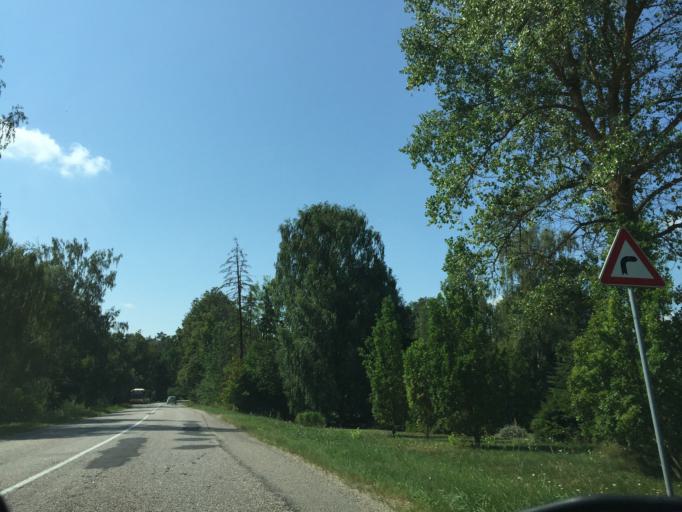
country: LV
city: Tervete
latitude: 56.4950
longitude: 23.4423
